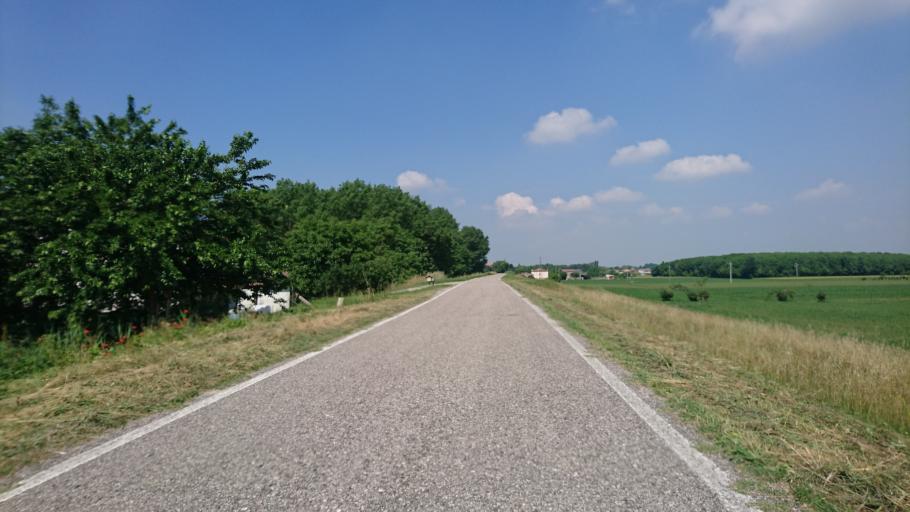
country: IT
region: Lombardy
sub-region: Provincia di Mantova
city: San Benedetto Po
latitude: 45.0778
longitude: 10.9721
